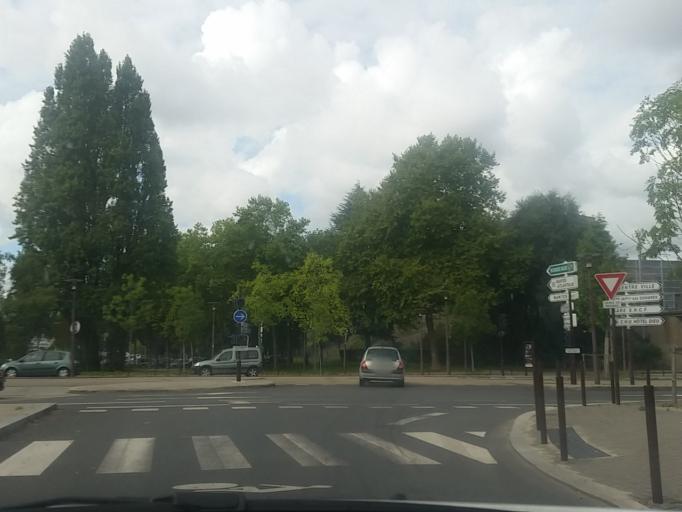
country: FR
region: Pays de la Loire
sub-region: Departement de la Loire-Atlantique
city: Nantes
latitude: 47.2053
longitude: -1.5377
